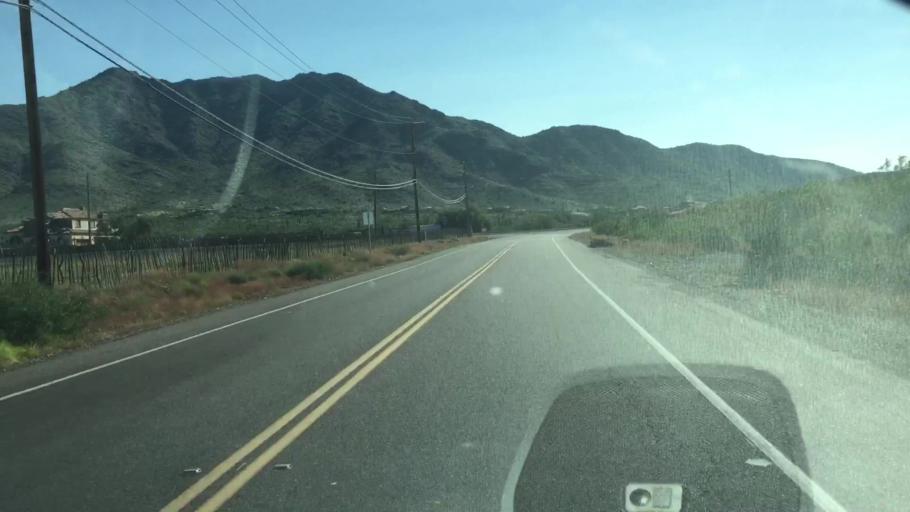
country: US
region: Arizona
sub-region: Maricopa County
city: Laveen
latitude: 33.3504
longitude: -112.1348
